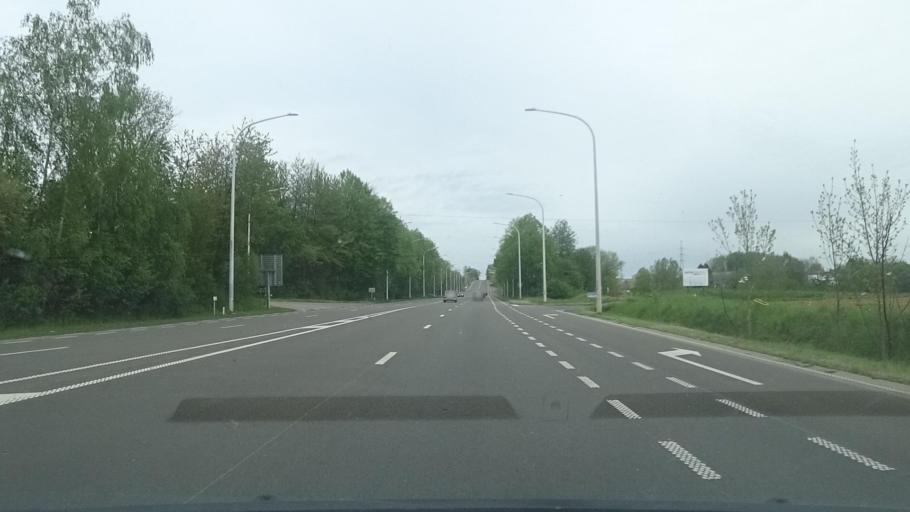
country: BE
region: Wallonia
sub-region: Province de Namur
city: Floreffe
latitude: 50.4985
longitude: 4.7843
